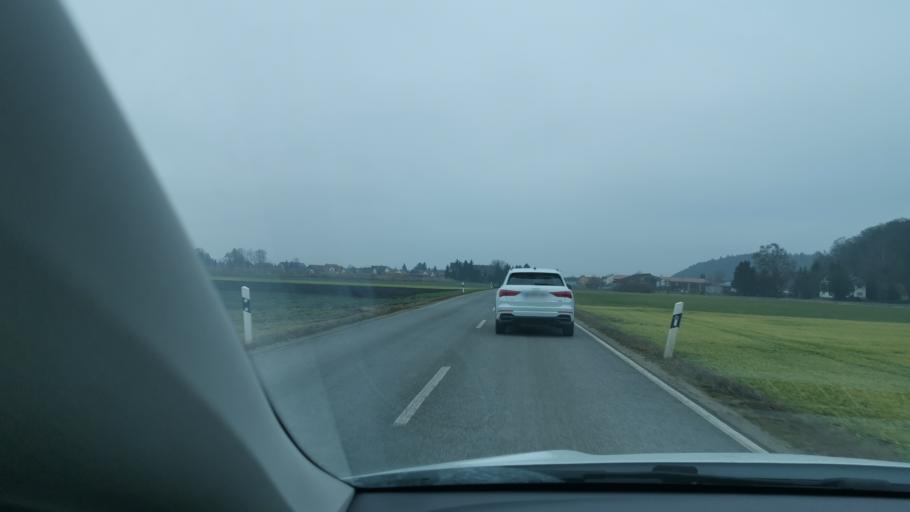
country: DE
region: Bavaria
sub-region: Swabia
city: Todtenweis
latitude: 48.5102
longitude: 10.9183
